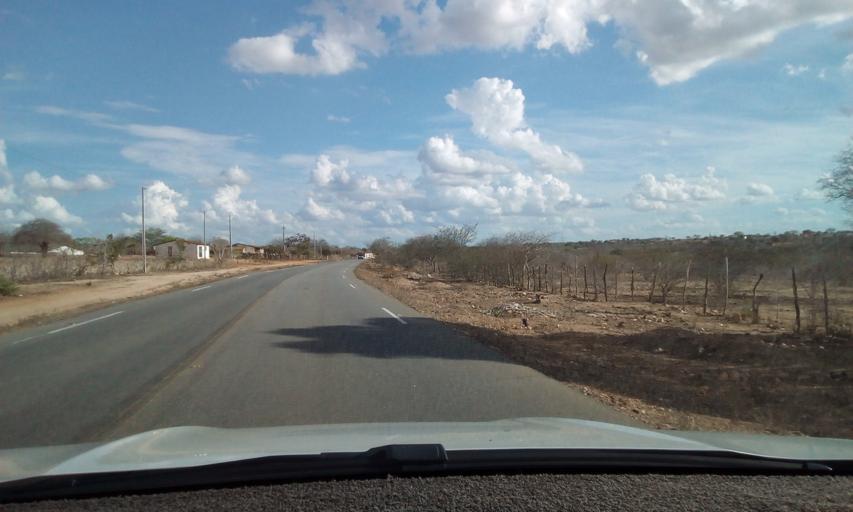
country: BR
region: Paraiba
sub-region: Soledade
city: Soledade
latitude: -6.9089
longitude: -36.3870
